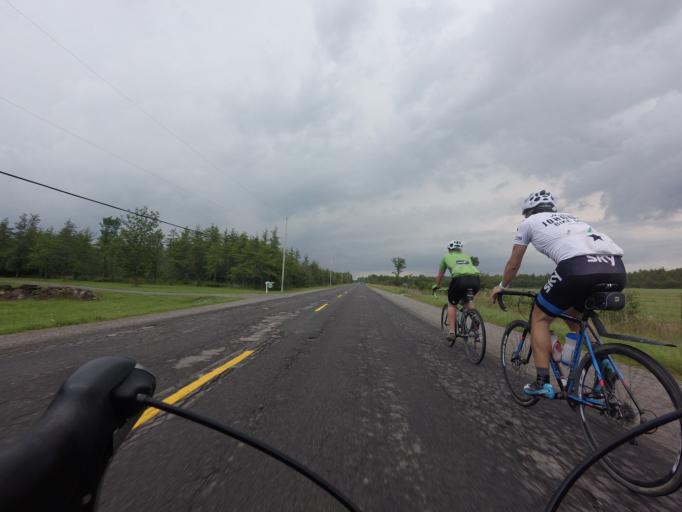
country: CA
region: Ontario
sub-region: Lanark County
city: Smiths Falls
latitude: 44.8831
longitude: -75.8172
